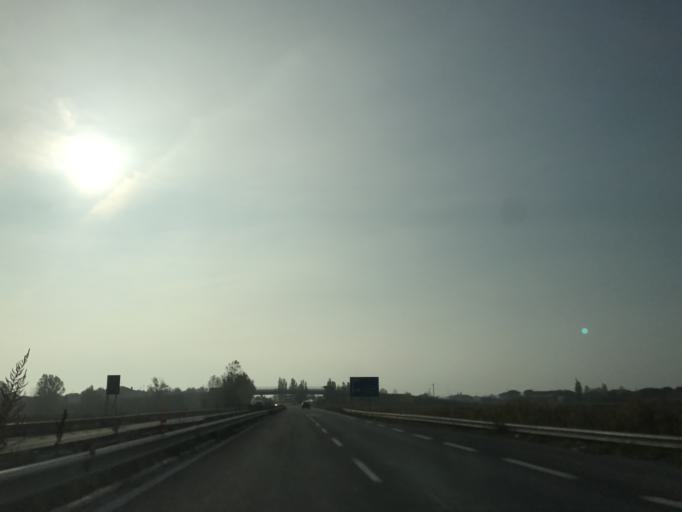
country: IT
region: Emilia-Romagna
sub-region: Forli-Cesena
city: San Mauro a Mare
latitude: 44.1531
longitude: 12.4414
